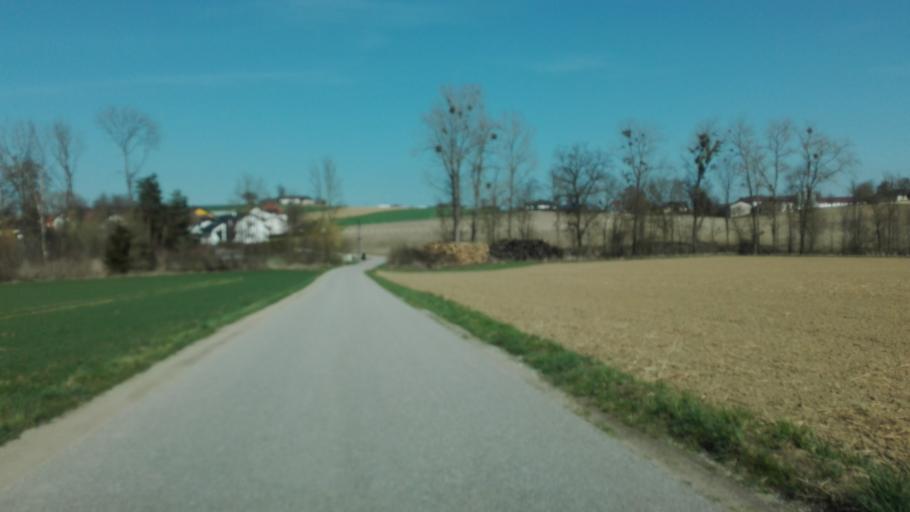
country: AT
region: Lower Austria
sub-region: Politischer Bezirk Amstetten
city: Ennsdorf
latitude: 48.2730
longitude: 14.5139
